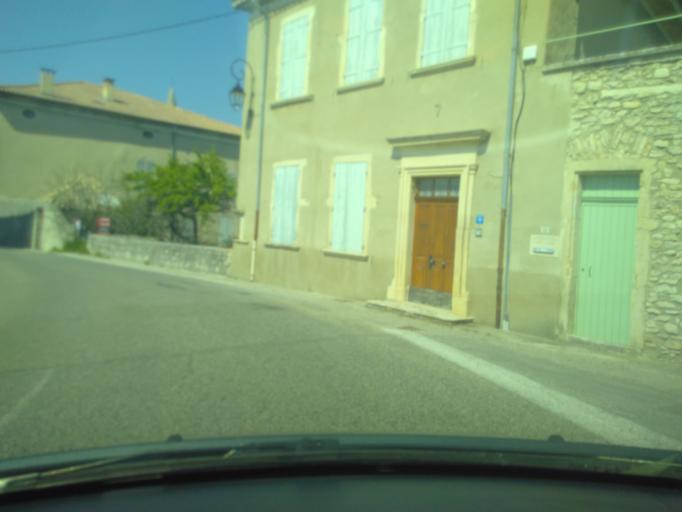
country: FR
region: Rhone-Alpes
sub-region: Departement de la Drome
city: Taulignan
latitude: 44.4418
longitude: 4.9807
